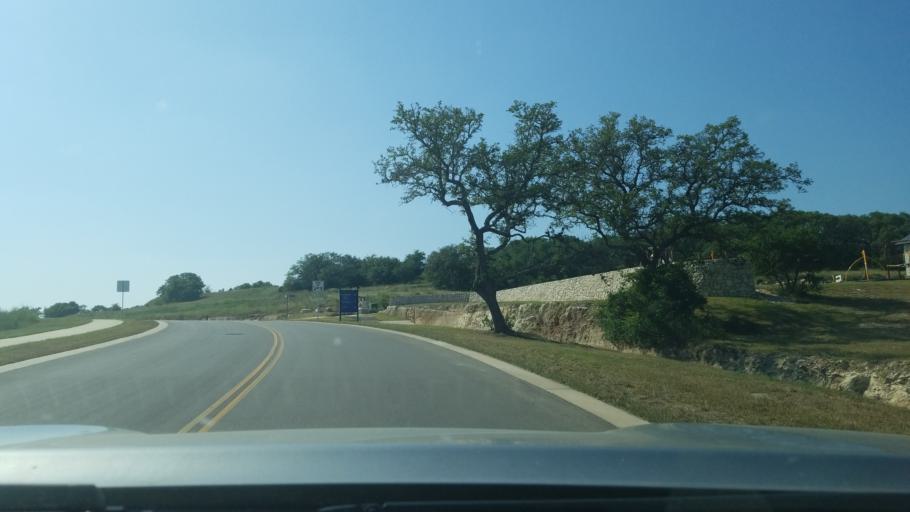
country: US
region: Texas
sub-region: Comal County
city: Bulverde
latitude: 29.7611
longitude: -98.4227
